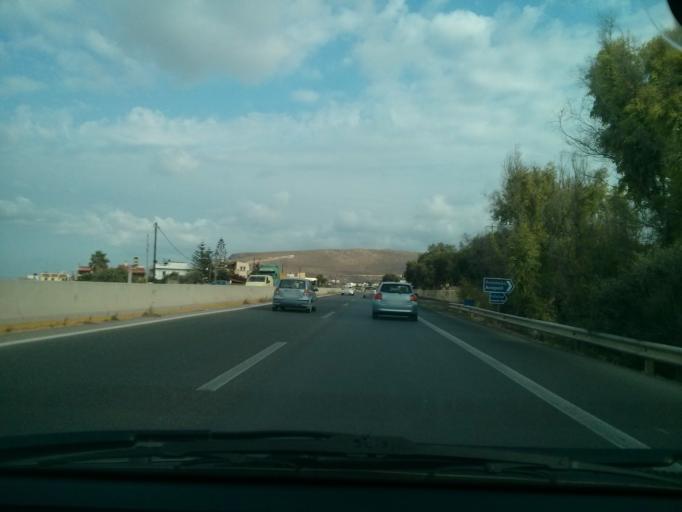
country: GR
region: Crete
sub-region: Nomos Irakleiou
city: Kokkini Hani
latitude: 35.3293
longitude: 25.2470
